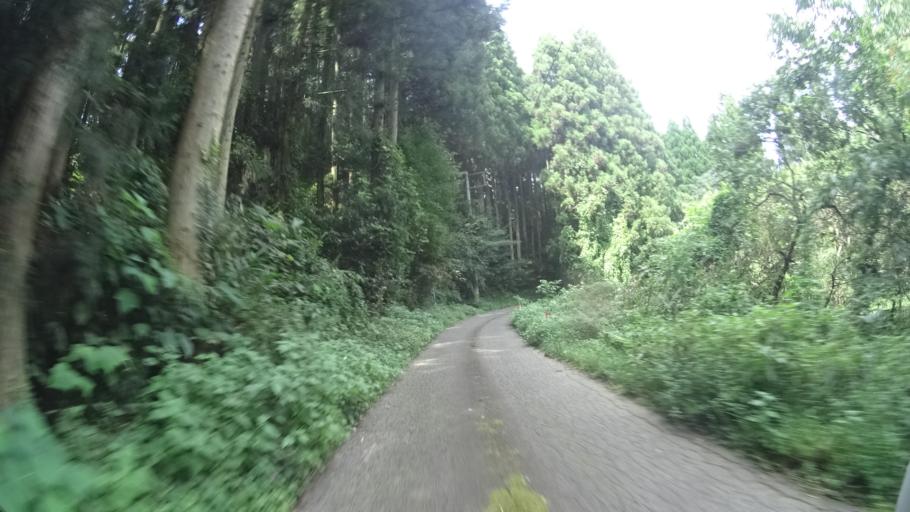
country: JP
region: Yamaguchi
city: Hagi
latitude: 34.4936
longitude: 131.5695
